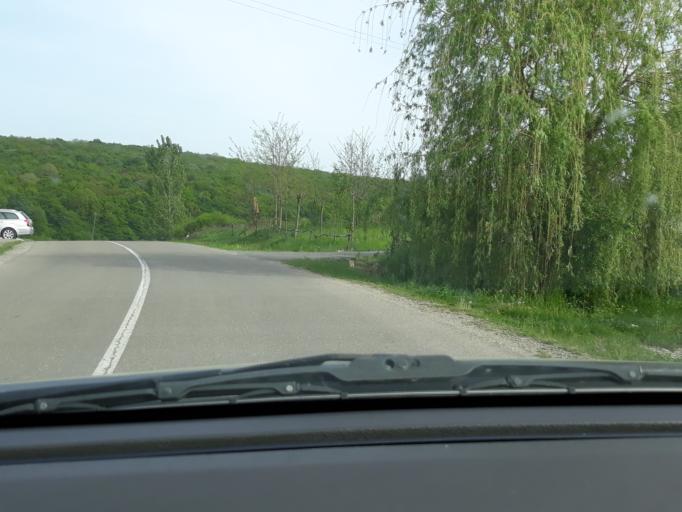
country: RO
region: Bihor
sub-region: Comuna Sanmartin
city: Sanmartin
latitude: 46.9864
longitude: 21.9981
